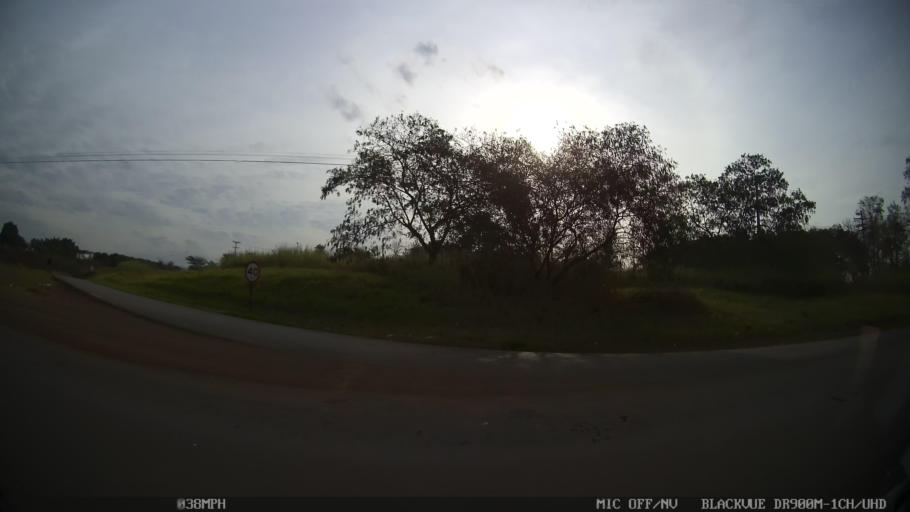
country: BR
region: Sao Paulo
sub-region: Piracicaba
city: Piracicaba
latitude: -22.7230
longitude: -47.5845
